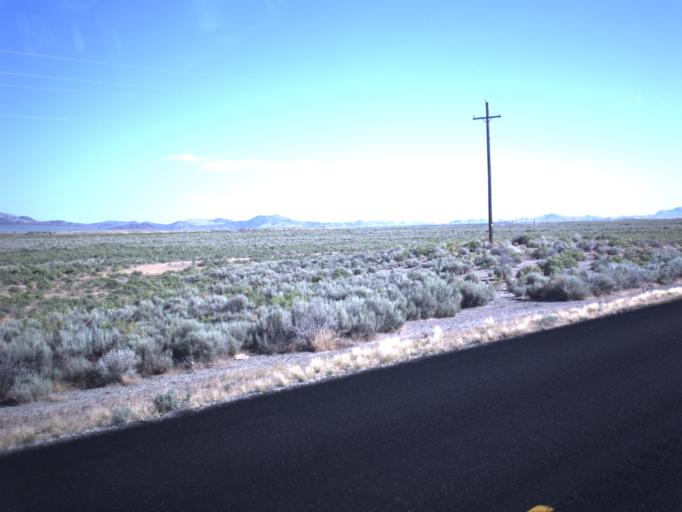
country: US
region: Utah
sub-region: Beaver County
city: Milford
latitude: 38.4506
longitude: -113.0074
